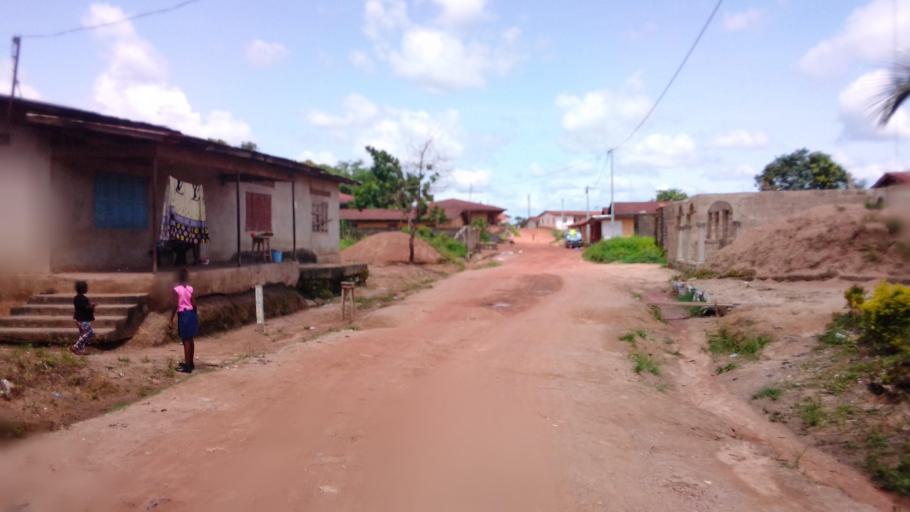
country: SL
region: Northern Province
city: Makeni
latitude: 8.8857
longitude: -12.0363
